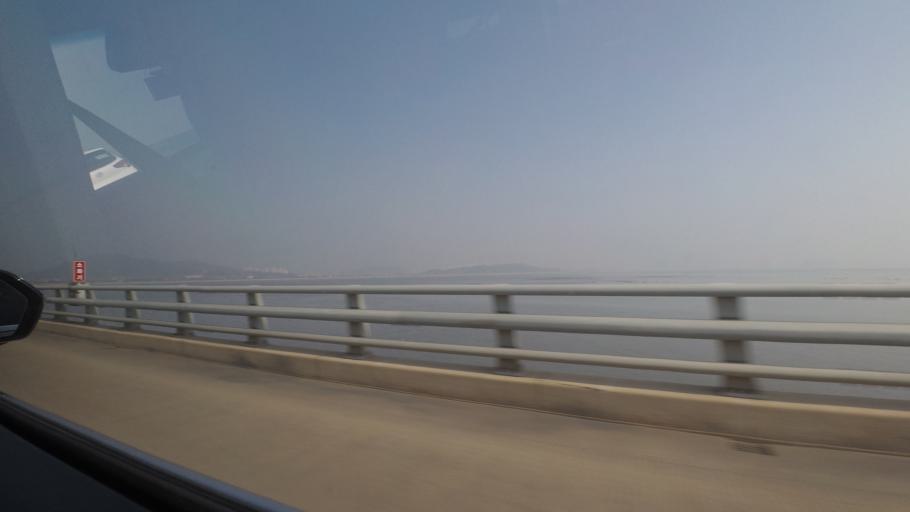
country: KR
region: Incheon
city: Incheon
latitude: 37.4532
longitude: 126.5262
